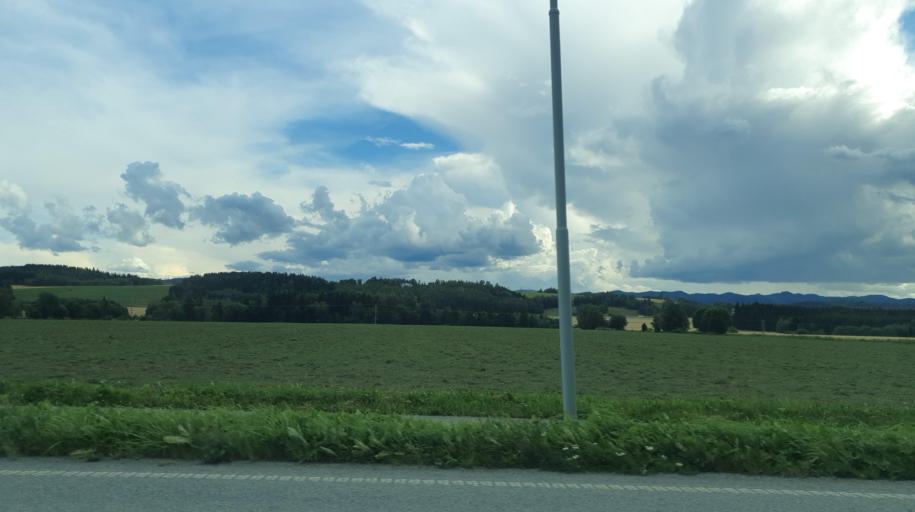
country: NO
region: Nord-Trondelag
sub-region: Levanger
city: Levanger
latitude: 63.7529
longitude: 11.3553
